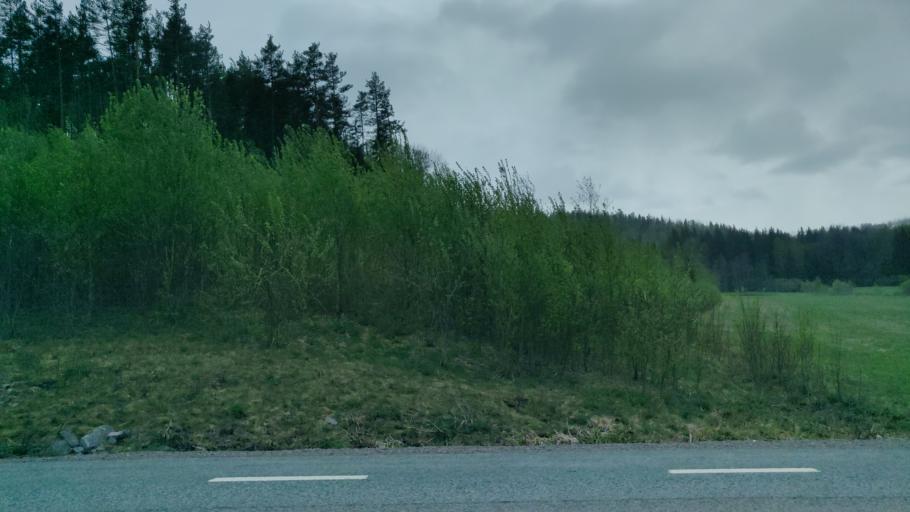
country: SE
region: Vaermland
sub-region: Forshaga Kommun
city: Deje
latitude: 59.6764
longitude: 13.4392
